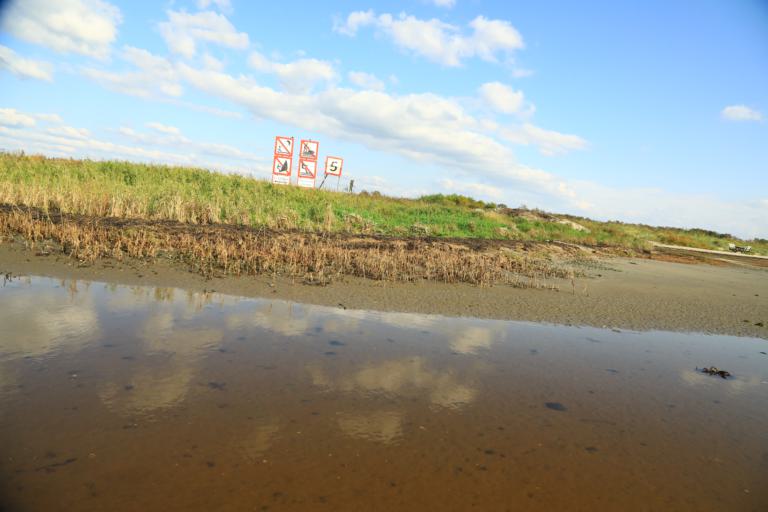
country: SE
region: Halland
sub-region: Varbergs Kommun
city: Tvaaker
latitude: 57.0104
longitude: 12.3435
